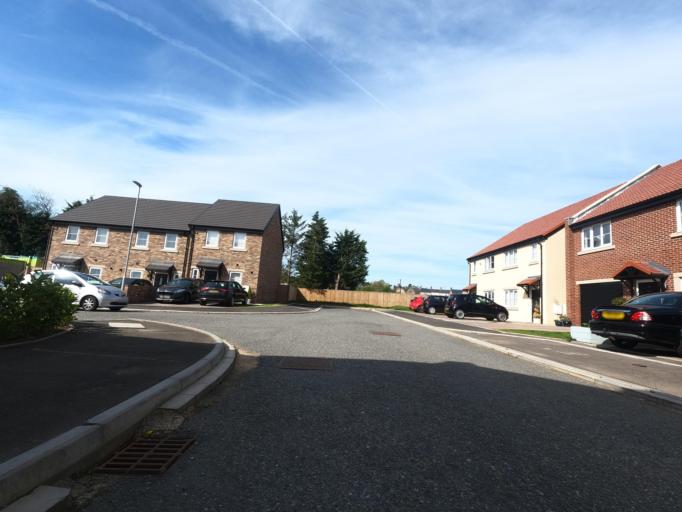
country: GB
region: England
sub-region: Northumberland
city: Stannington
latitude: 55.1279
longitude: -1.6574
